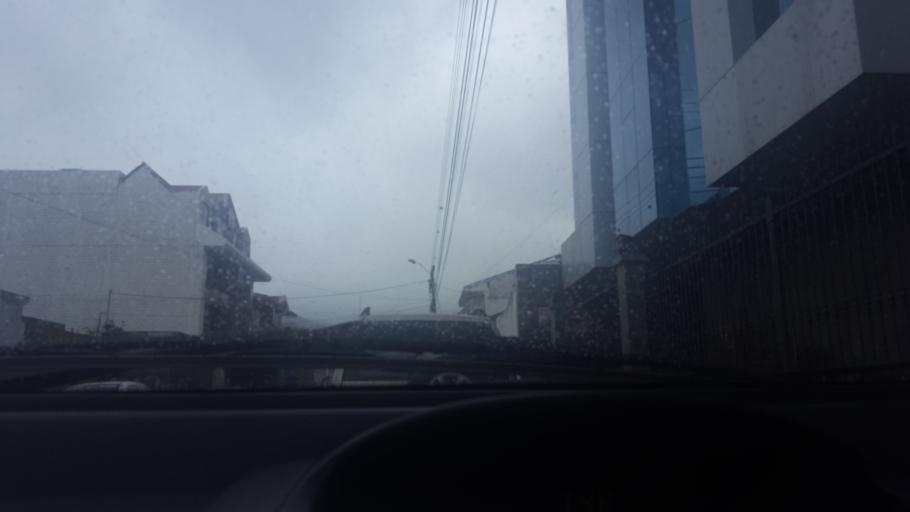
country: EC
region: Loja
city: Loja
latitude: -4.0032
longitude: -79.1995
